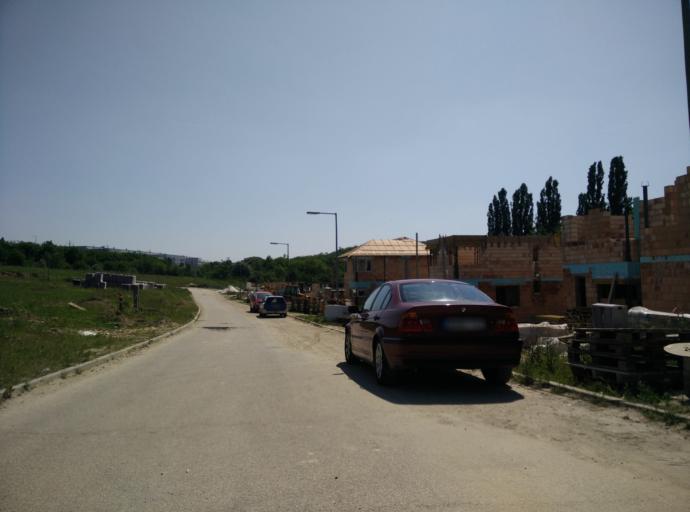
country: HU
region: Pest
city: Biatorbagy
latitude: 47.4713
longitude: 18.8425
